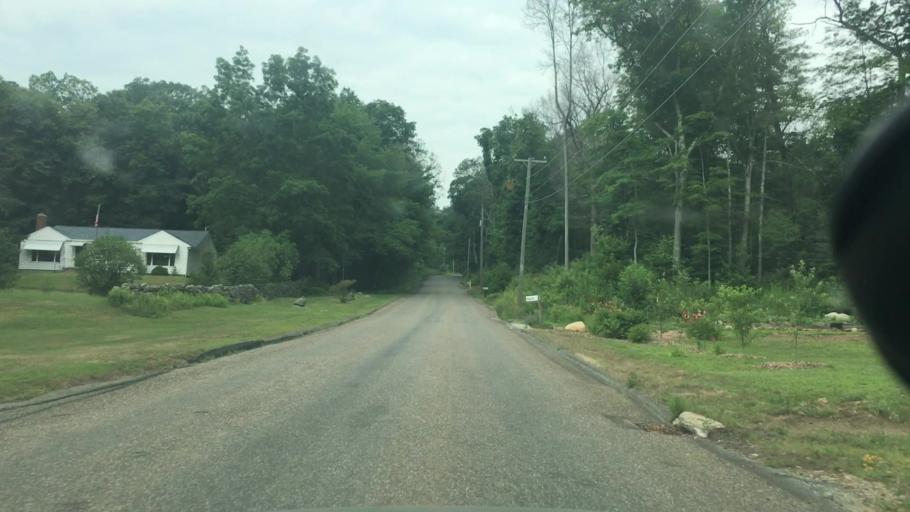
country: US
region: Connecticut
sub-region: Tolland County
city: Stafford
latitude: 41.9875
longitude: -72.2966
